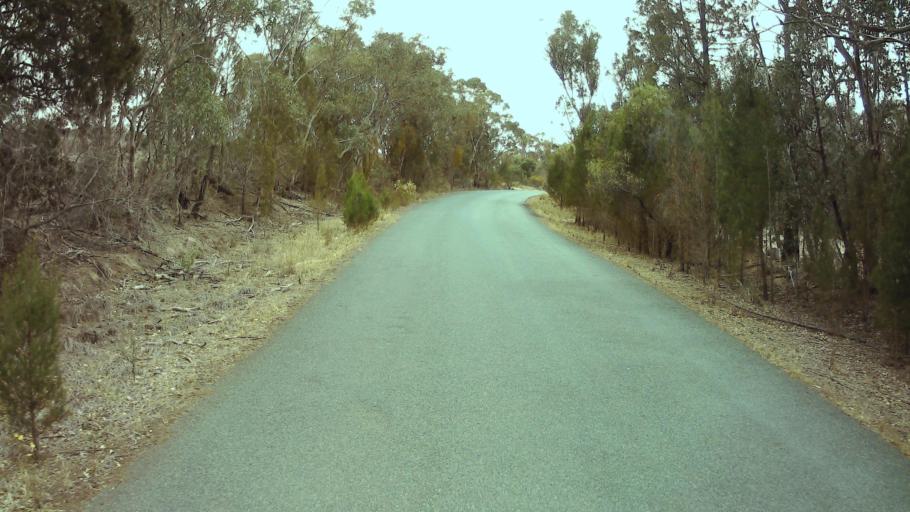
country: AU
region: New South Wales
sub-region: Weddin
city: Grenfell
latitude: -33.8854
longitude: 148.1505
